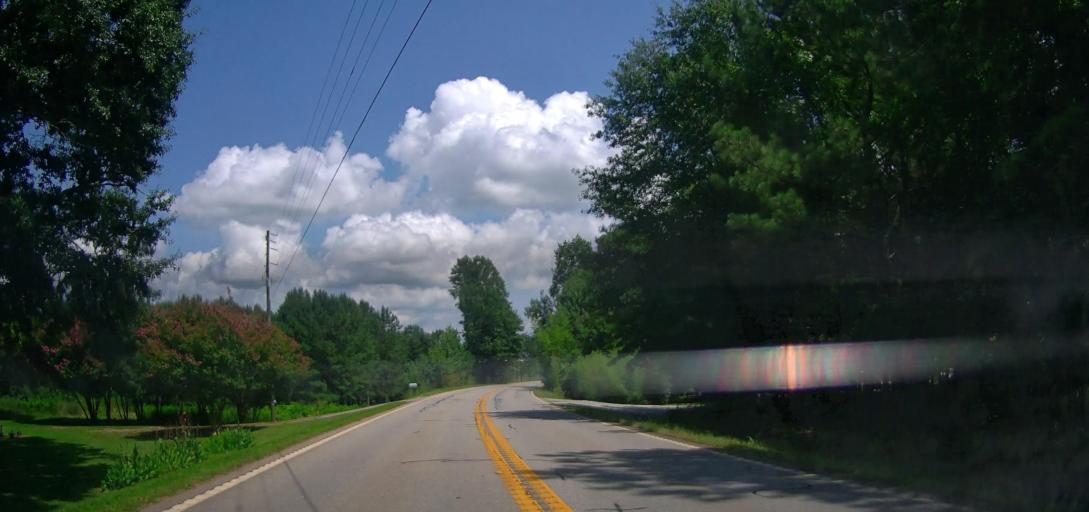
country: US
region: Georgia
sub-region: Carroll County
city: Bowdon
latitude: 33.3748
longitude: -85.2380
